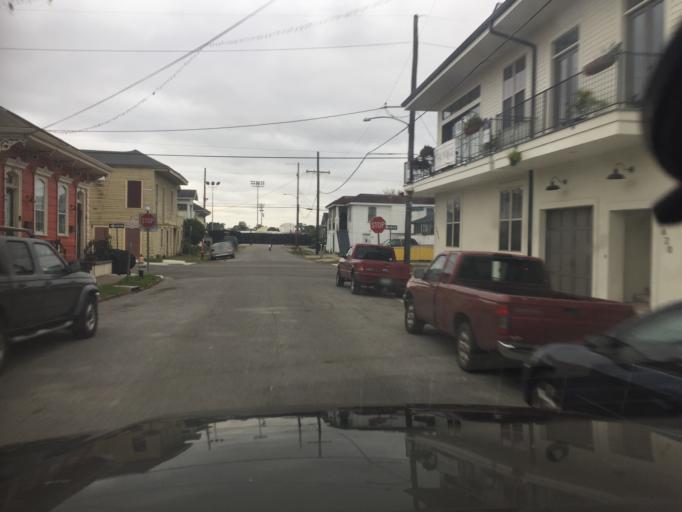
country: US
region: Louisiana
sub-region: Orleans Parish
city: New Orleans
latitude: 29.9806
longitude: -90.0815
